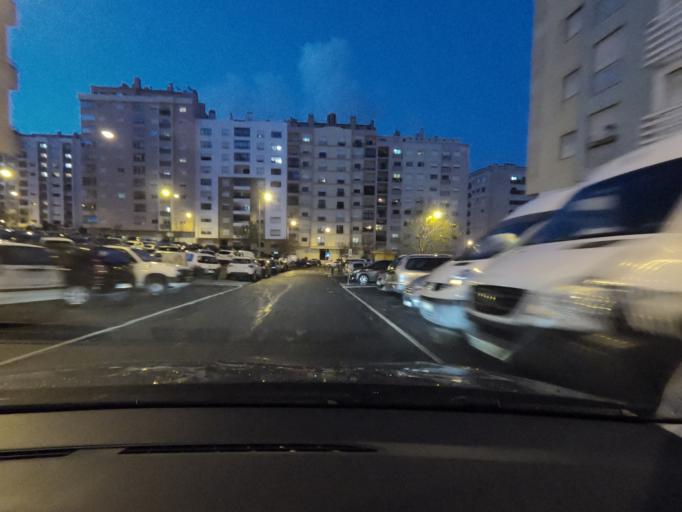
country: PT
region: Lisbon
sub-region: Sintra
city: Cacem
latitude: 38.7485
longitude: -9.2983
